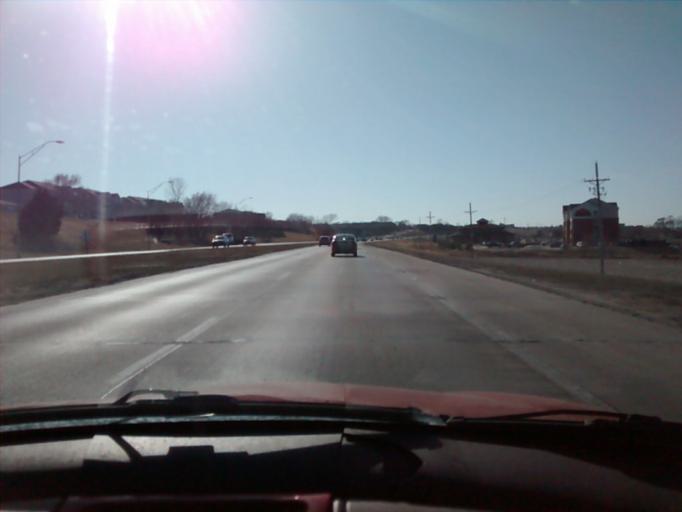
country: US
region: Nebraska
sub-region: Sarpy County
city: Offutt Air Force Base
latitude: 41.1382
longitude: -95.9504
